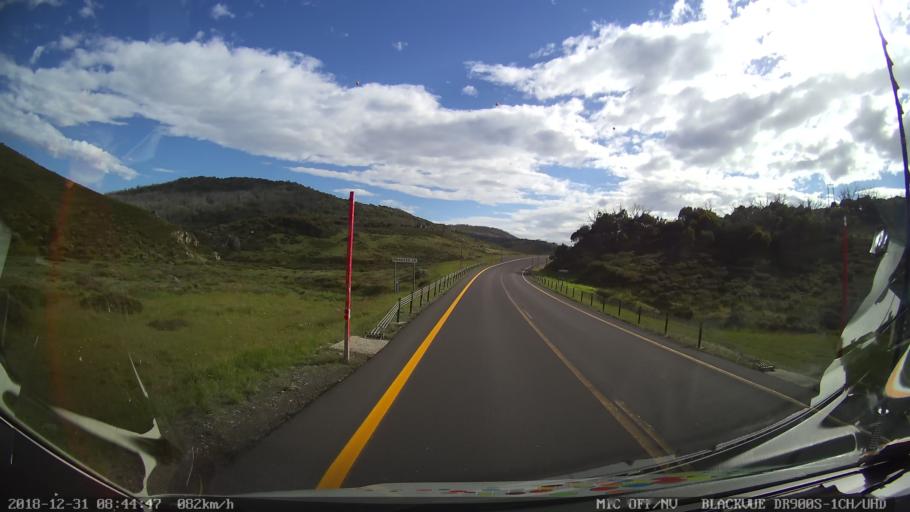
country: AU
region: New South Wales
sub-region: Snowy River
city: Jindabyne
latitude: -36.3807
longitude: 148.4579
